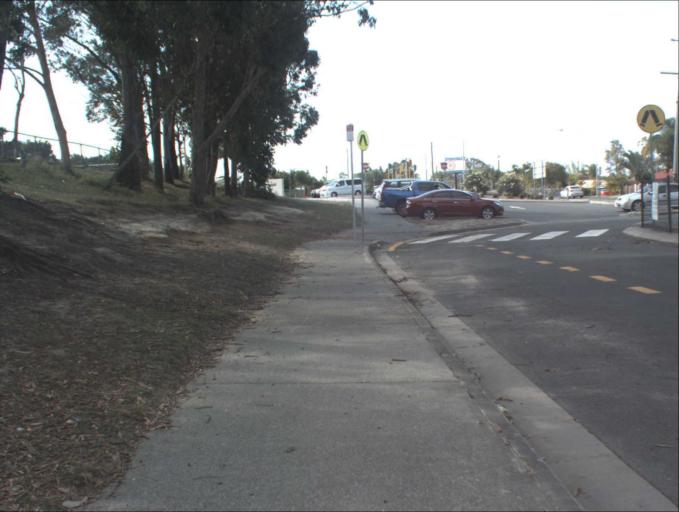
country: AU
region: Queensland
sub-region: Logan
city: Logan Reserve
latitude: -27.6924
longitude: 153.0825
